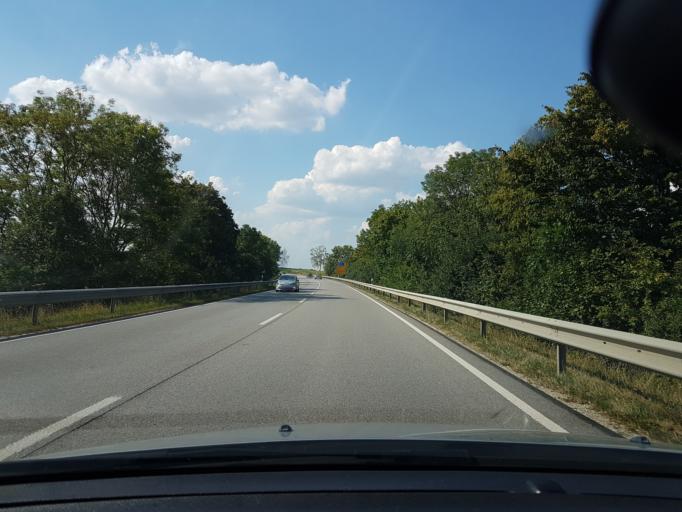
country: DE
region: Bavaria
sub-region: Lower Bavaria
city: Kumhausen
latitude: 48.5136
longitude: 12.2064
